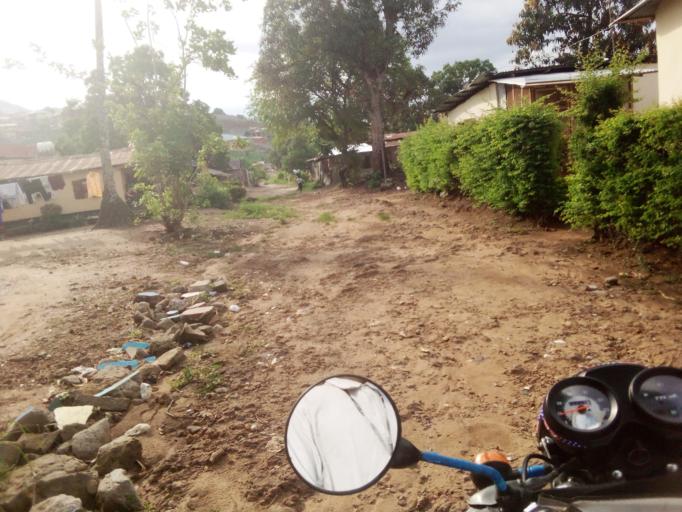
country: SL
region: Western Area
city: Waterloo
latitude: 8.3427
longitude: -13.0720
